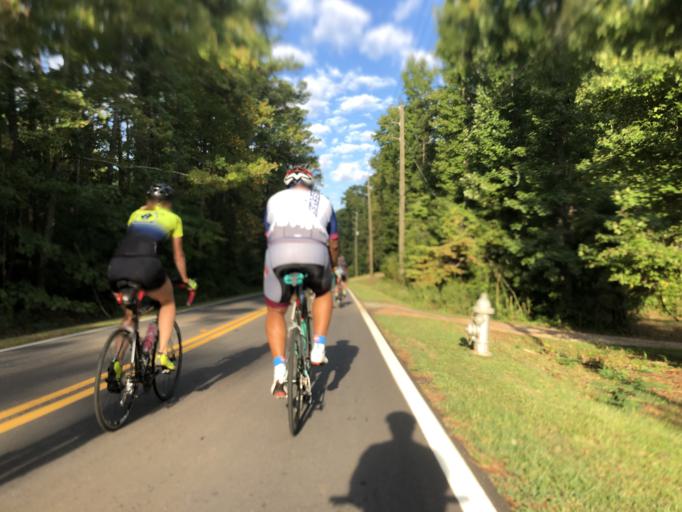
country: US
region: Georgia
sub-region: Fulton County
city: Palmetto
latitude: 33.5741
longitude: -84.6570
